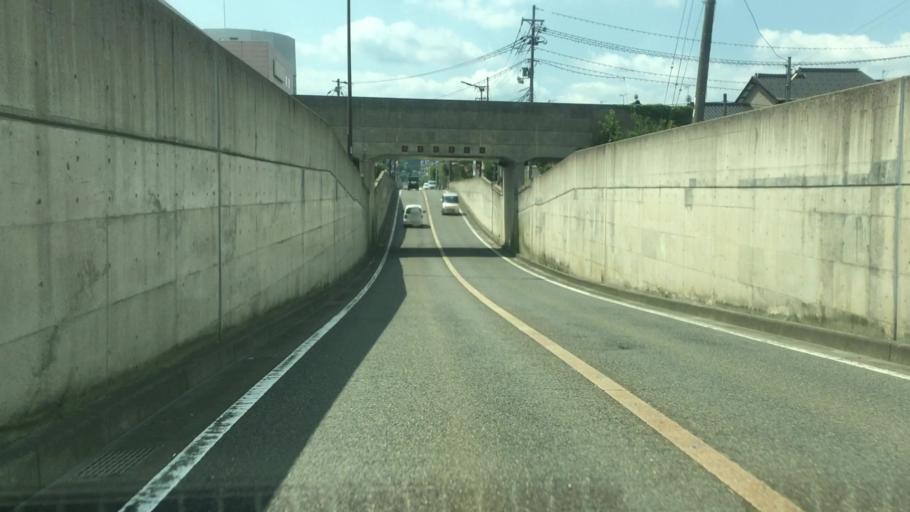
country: JP
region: Hyogo
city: Toyooka
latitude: 35.5518
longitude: 134.8155
